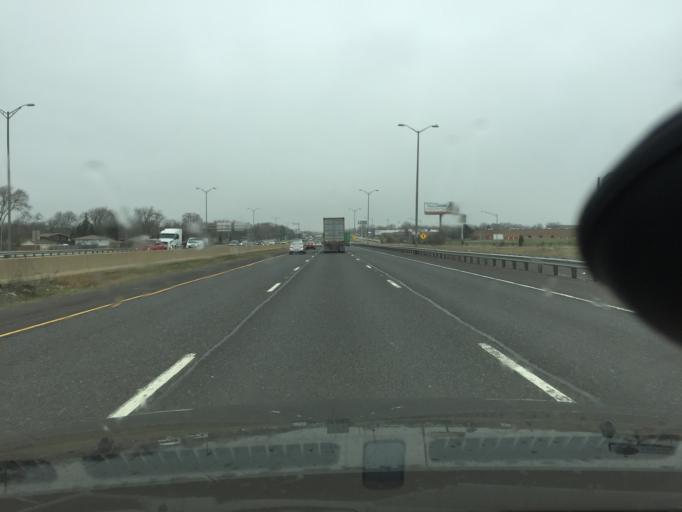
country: US
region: Illinois
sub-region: Cook County
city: Country Club Hills
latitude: 41.5884
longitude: -87.7263
